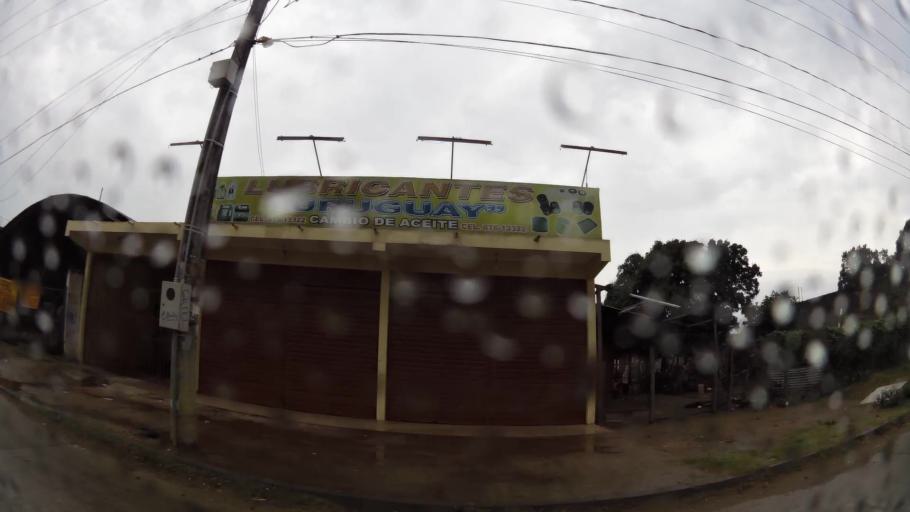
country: BO
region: Santa Cruz
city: Santa Cruz de la Sierra
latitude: -17.8023
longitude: -63.1281
